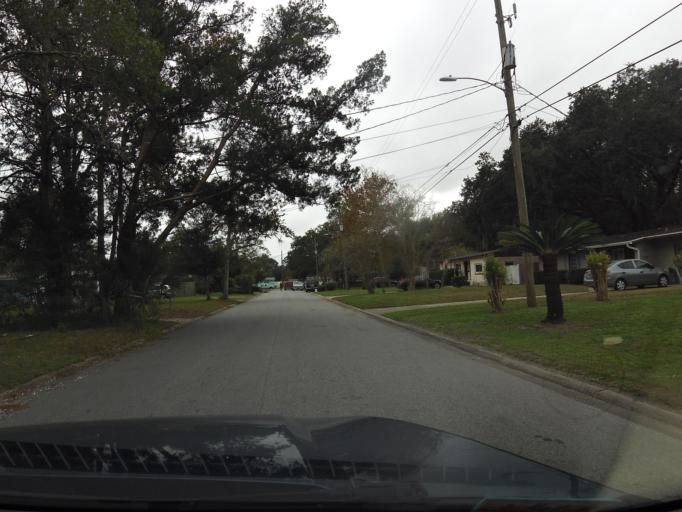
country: US
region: Florida
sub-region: Duval County
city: Jacksonville
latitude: 30.2849
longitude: -81.5977
